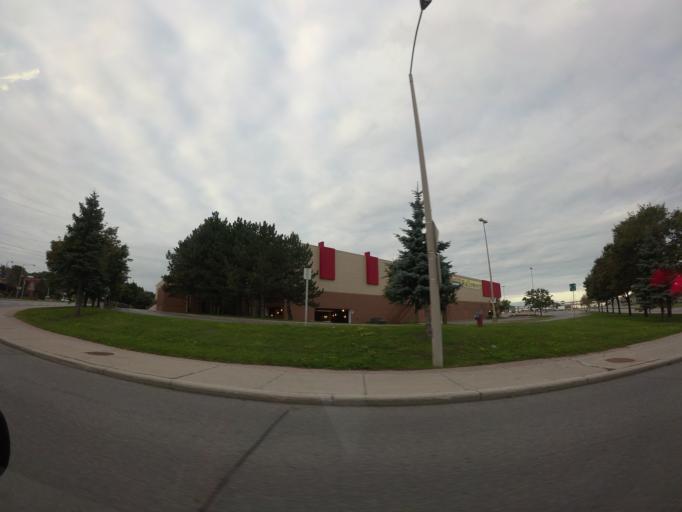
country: CA
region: Quebec
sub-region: Outaouais
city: Gatineau
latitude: 45.4805
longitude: -75.5139
